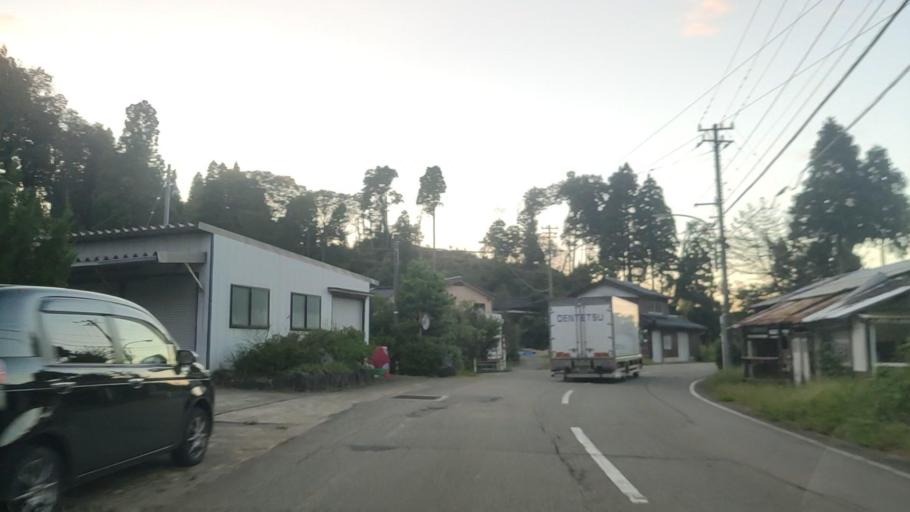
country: JP
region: Ishikawa
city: Tsubata
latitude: 36.6462
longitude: 136.7632
